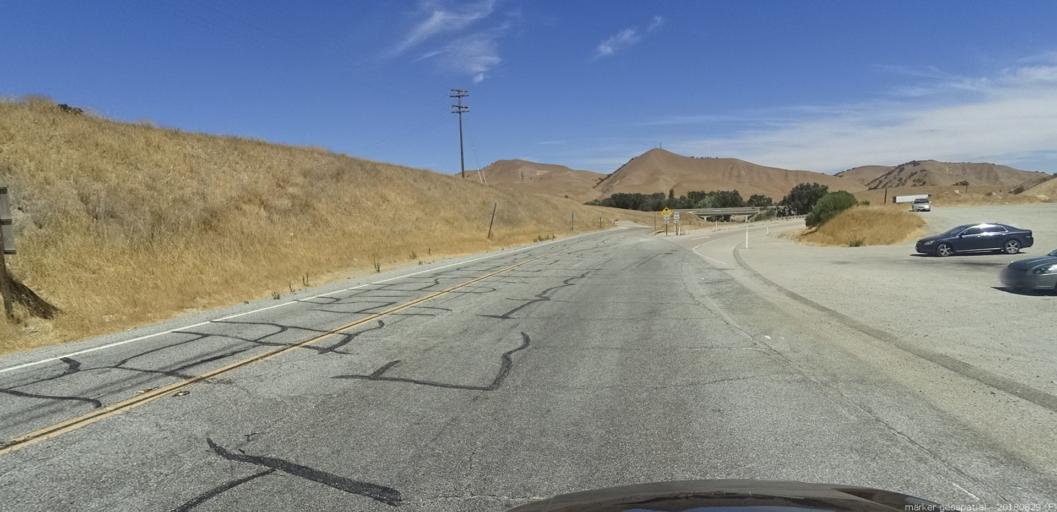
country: US
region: California
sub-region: San Luis Obispo County
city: Lake Nacimiento
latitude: 35.8729
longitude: -120.8382
